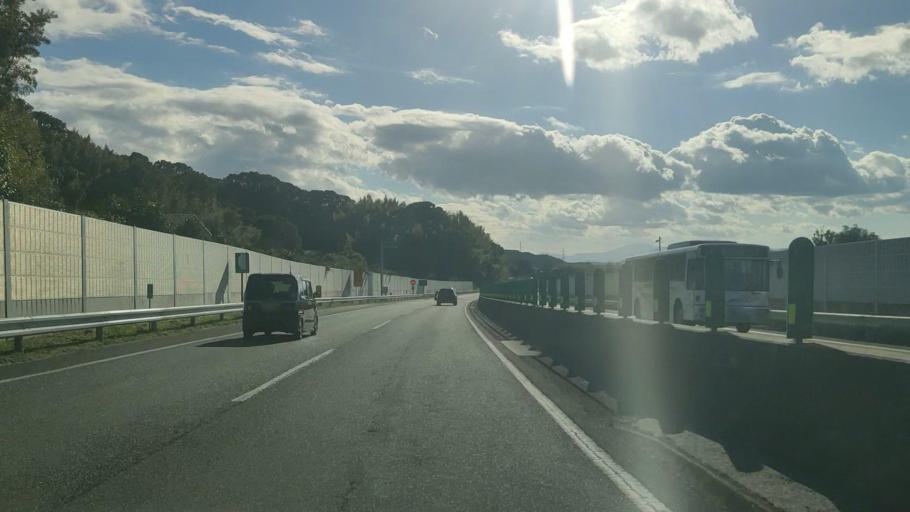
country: JP
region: Fukuoka
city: Nakama
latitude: 33.8294
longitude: 130.7653
